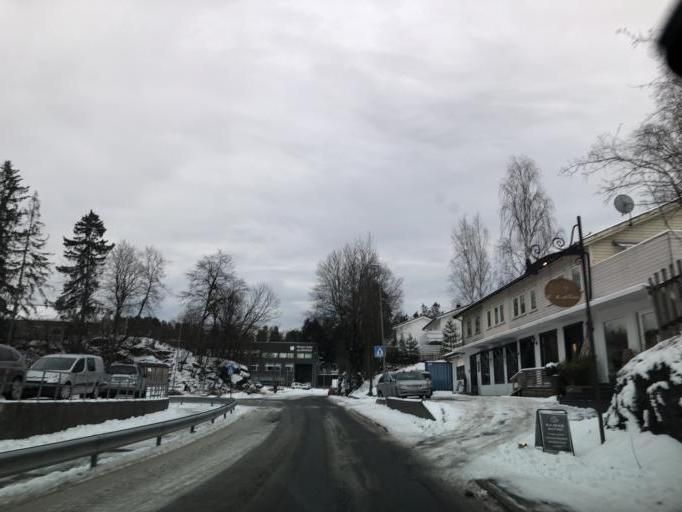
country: NO
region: Akershus
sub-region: Baerum
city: Sandvika
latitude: 59.8709
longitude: 10.5165
